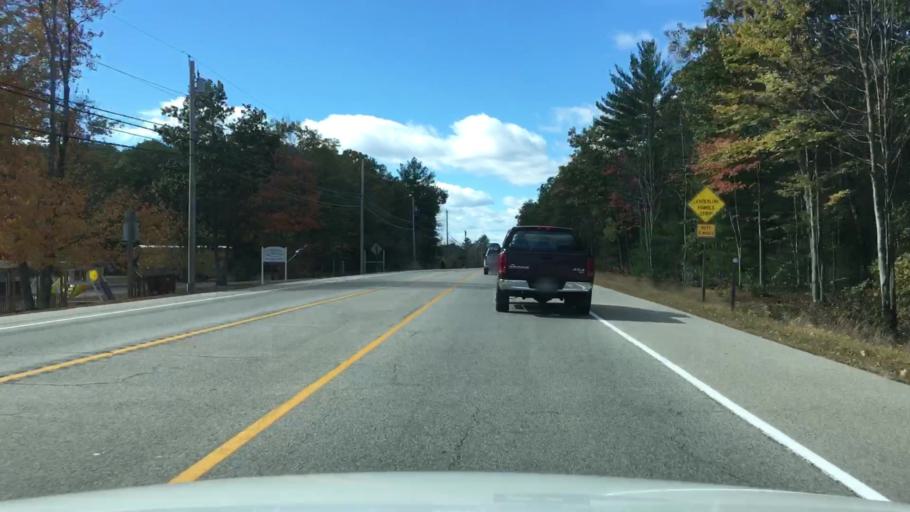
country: US
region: Maine
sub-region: York County
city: West Kennebunk
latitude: 43.4794
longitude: -70.6071
